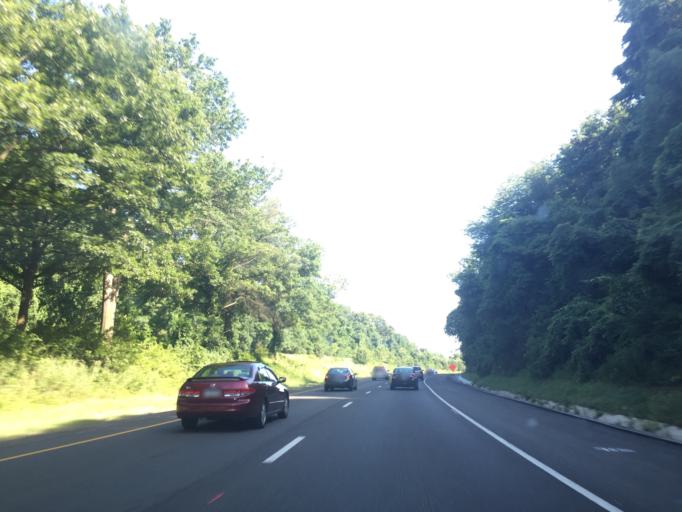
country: US
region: Maryland
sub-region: Baltimore County
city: Hunt Valley
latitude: 39.5298
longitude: -76.6619
